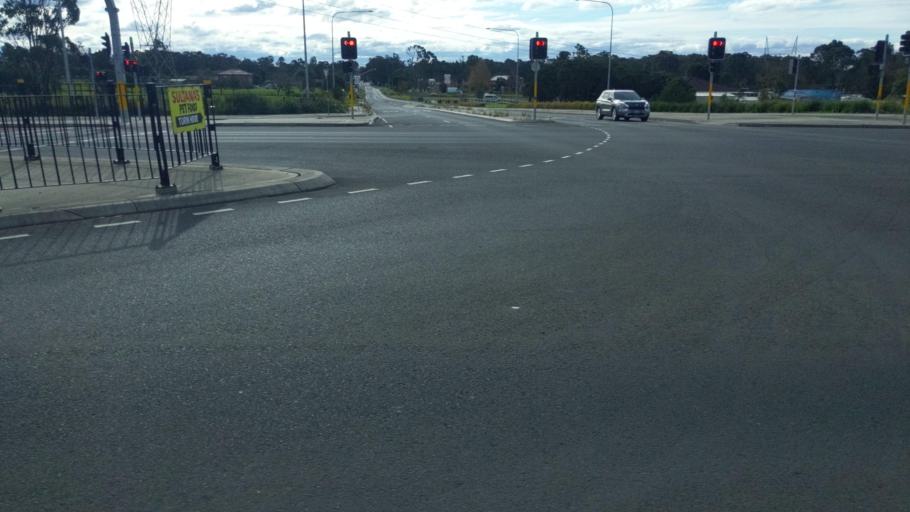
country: AU
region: New South Wales
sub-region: Blacktown
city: Riverstone
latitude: -33.7040
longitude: 150.8583
